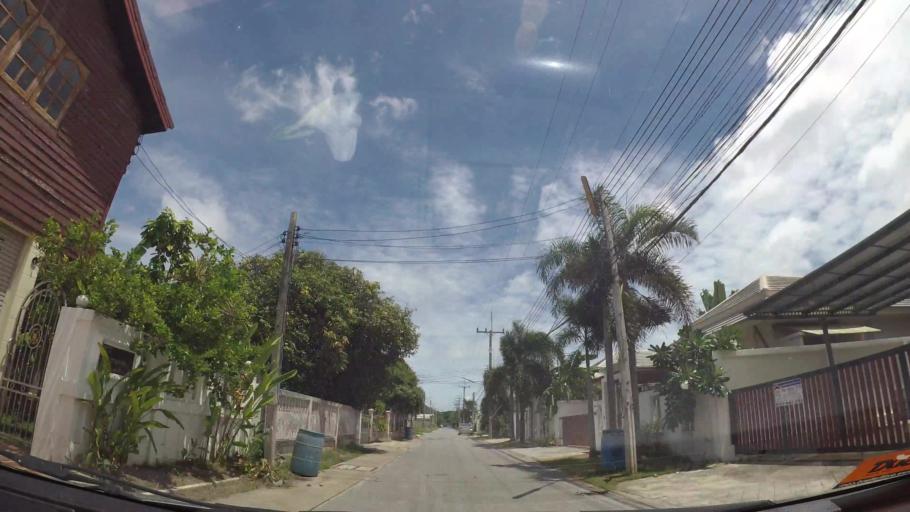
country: TH
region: Chon Buri
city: Sattahip
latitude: 12.7412
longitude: 100.8932
